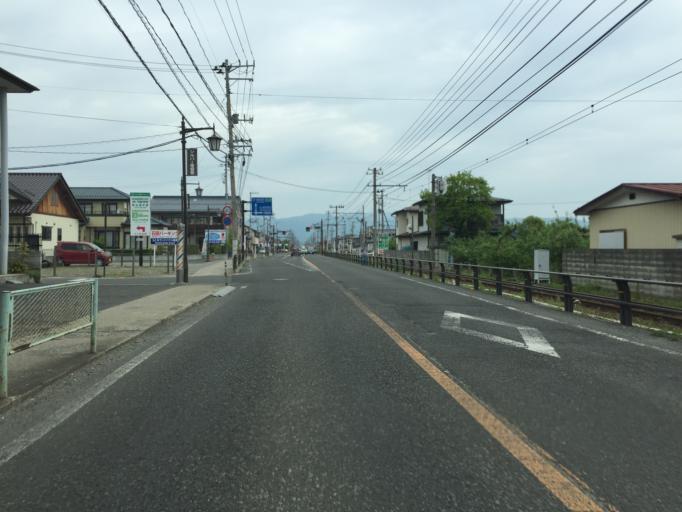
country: JP
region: Fukushima
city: Fukushima-shi
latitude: 37.7888
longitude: 140.4398
